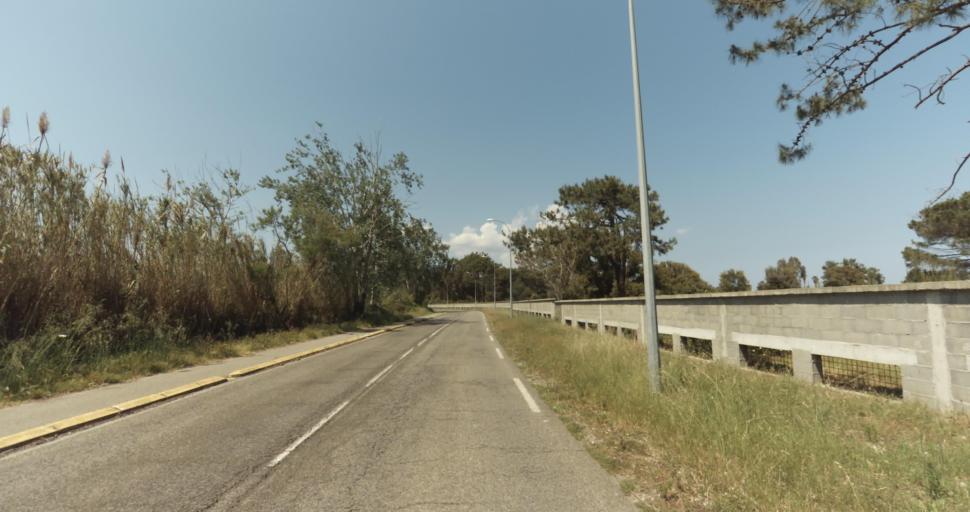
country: FR
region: Corsica
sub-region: Departement de la Haute-Corse
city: Biguglia
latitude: 42.6210
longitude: 9.4742
